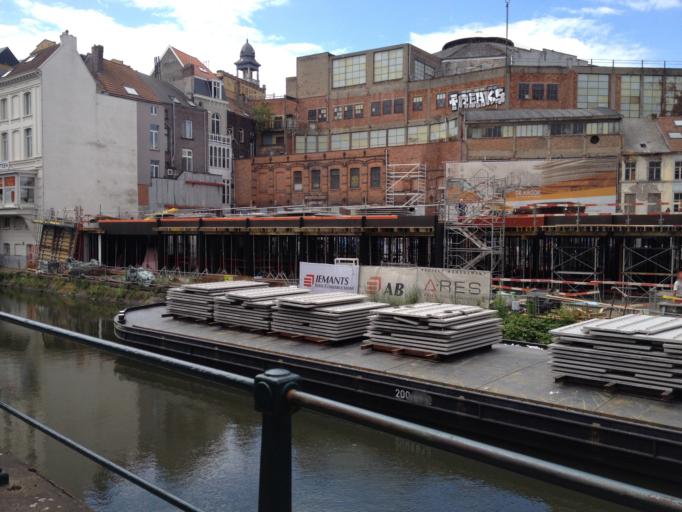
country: BE
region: Flanders
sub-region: Provincie Oost-Vlaanderen
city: Gent
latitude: 51.0484
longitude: 3.7294
